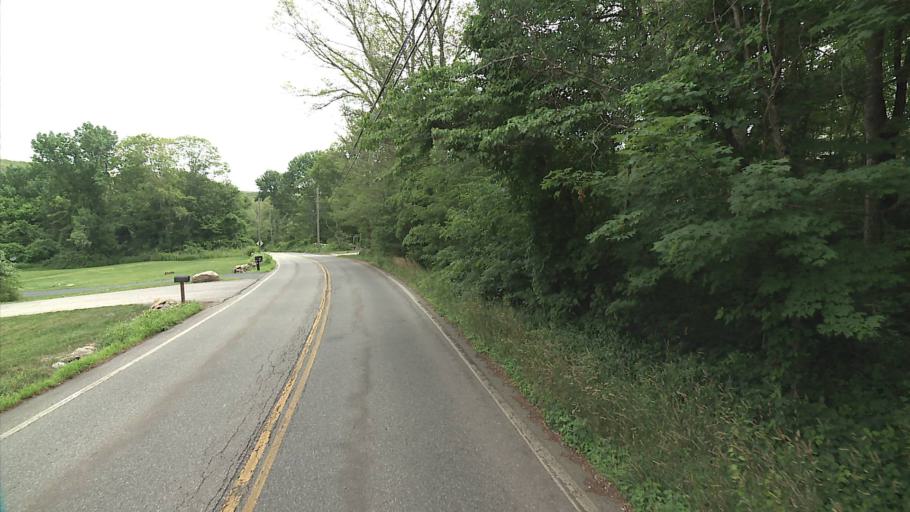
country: US
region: Connecticut
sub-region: New London County
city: Ledyard Center
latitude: 41.4475
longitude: -71.9802
